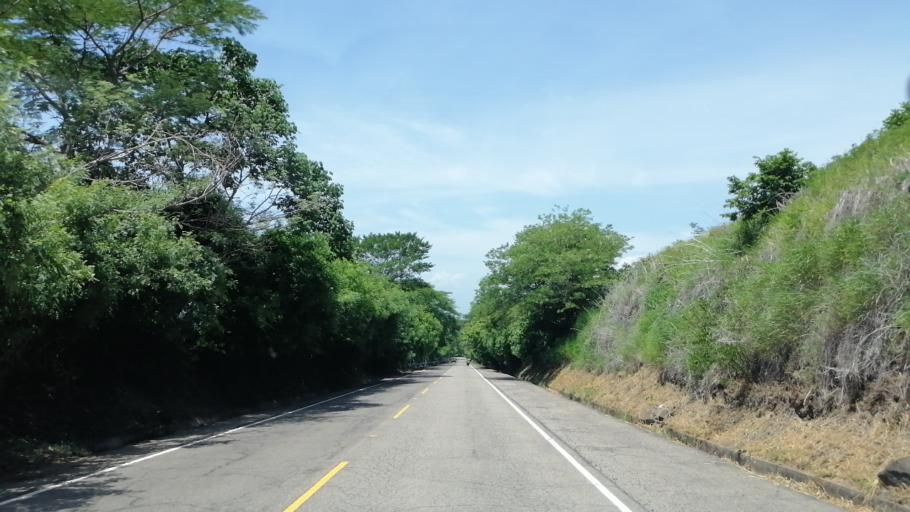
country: SV
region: Chalatenango
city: Nueva Concepcion
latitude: 14.1539
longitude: -89.3052
